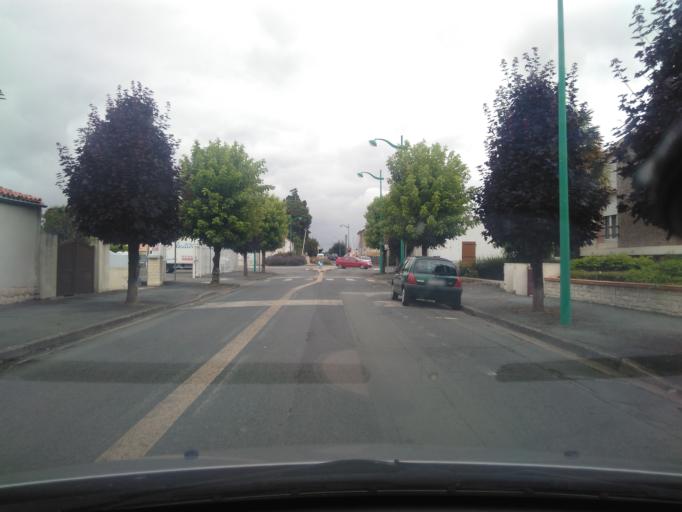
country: FR
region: Pays de la Loire
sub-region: Departement de la Vendee
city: Lucon
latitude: 46.4634
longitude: -1.1714
